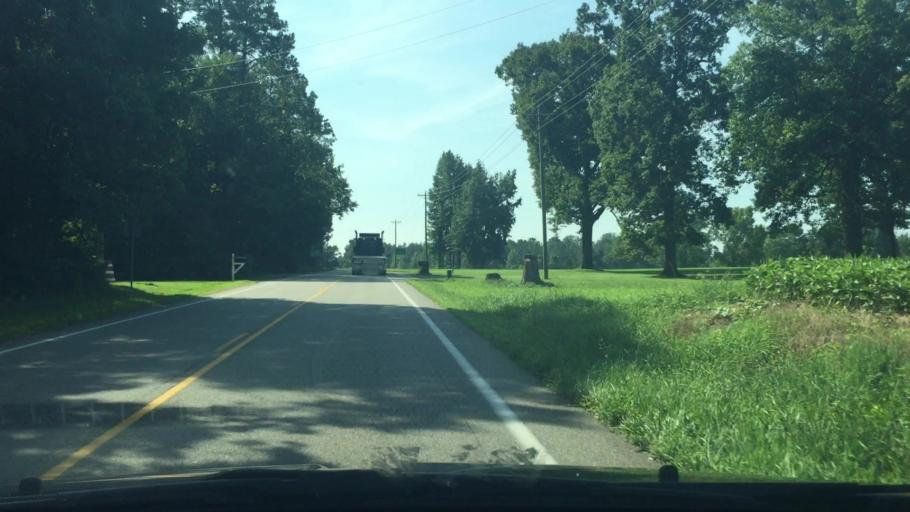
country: US
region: Virginia
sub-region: Sussex County
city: Sussex
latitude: 37.0386
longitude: -77.3091
